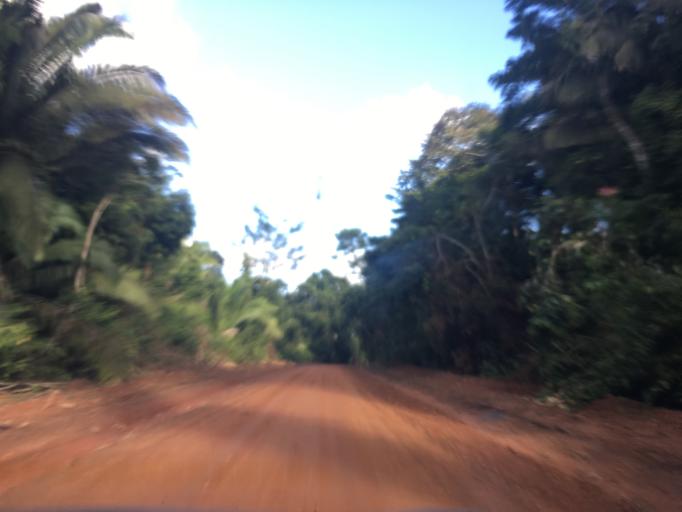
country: BZ
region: Stann Creek
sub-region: Dangriga
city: Dangriga
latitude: 16.7994
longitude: -88.4061
